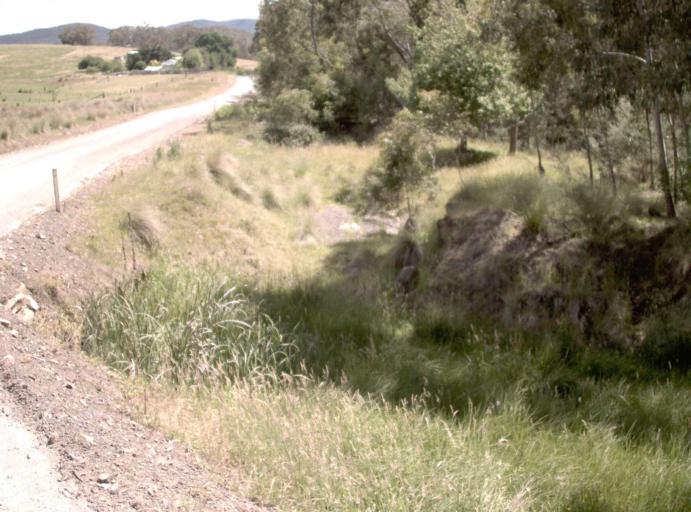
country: AU
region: New South Wales
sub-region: Bombala
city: Bombala
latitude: -37.1313
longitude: 148.6664
